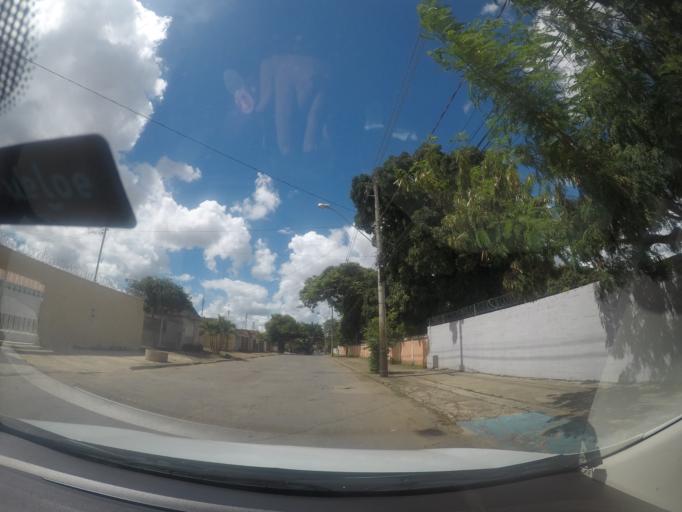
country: BR
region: Goias
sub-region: Goiania
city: Goiania
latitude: -16.6629
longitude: -49.2986
